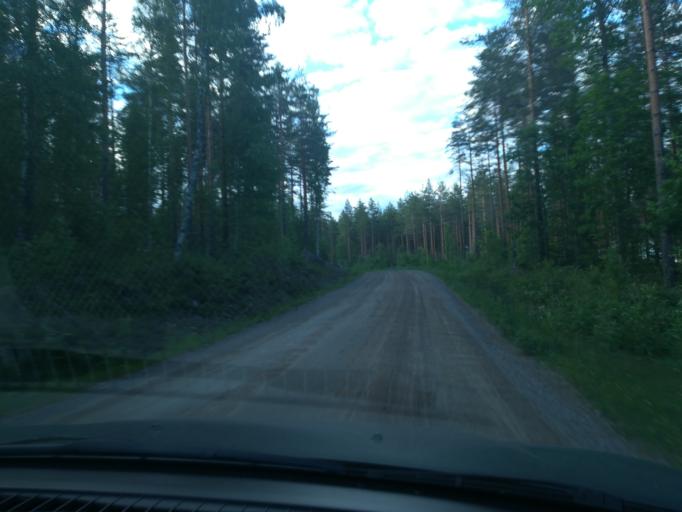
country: FI
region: Southern Savonia
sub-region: Mikkeli
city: Puumala
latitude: 61.5824
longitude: 28.1658
